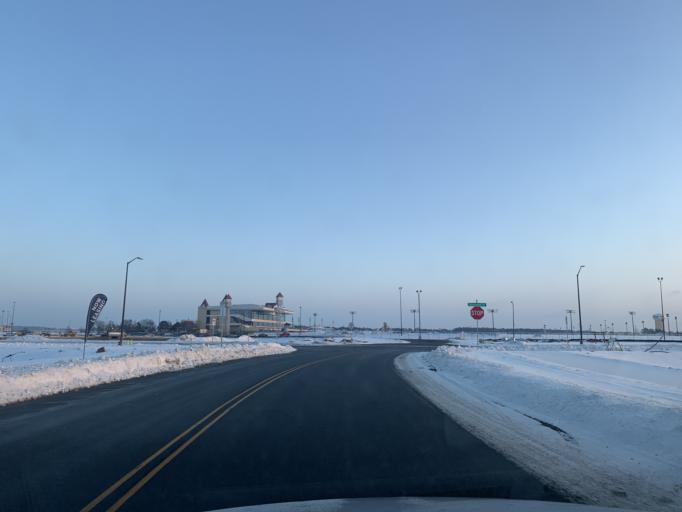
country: US
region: Minnesota
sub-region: Scott County
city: Shakopee
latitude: 44.7862
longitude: -93.4855
